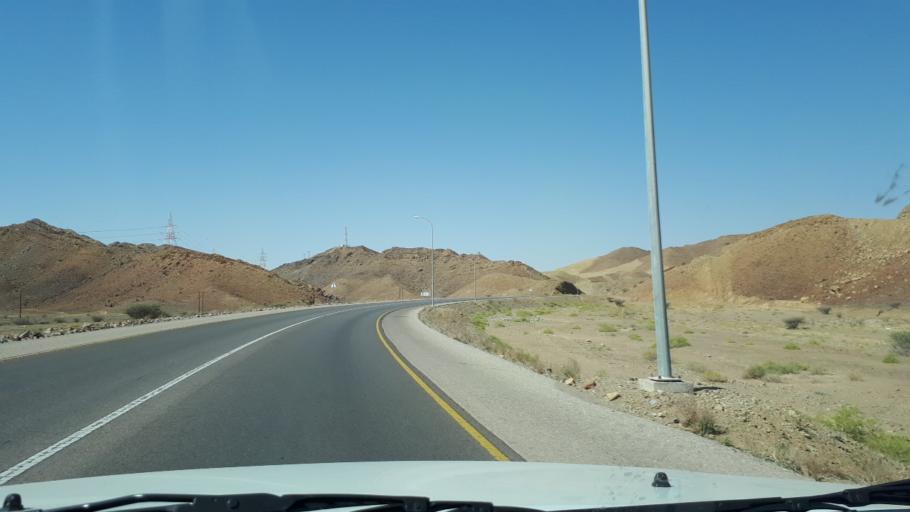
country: OM
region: Ash Sharqiyah
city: Sur
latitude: 22.3402
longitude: 59.3141
